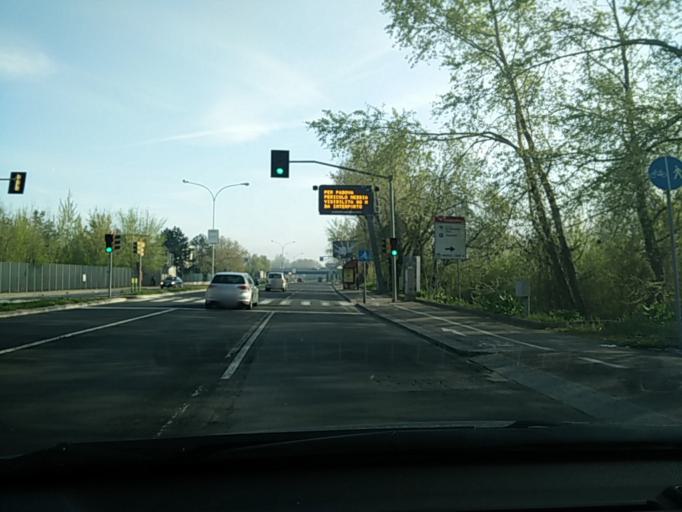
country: IT
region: Emilia-Romagna
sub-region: Provincia di Bologna
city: Bologna
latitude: 44.5202
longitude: 11.3620
